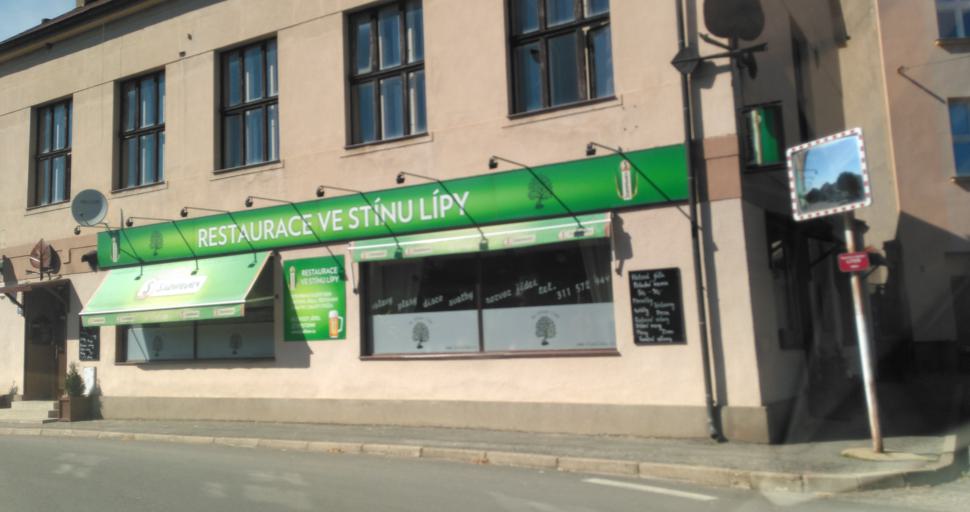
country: CZ
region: Central Bohemia
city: Revnice
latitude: 49.9049
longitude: 14.1473
